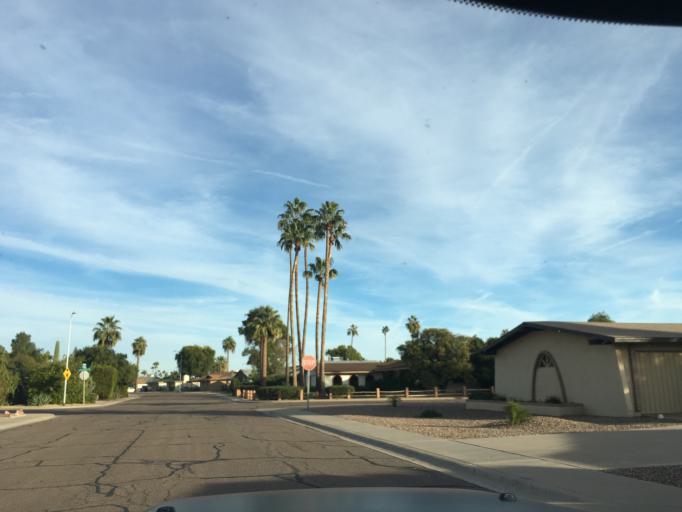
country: US
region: Arizona
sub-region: Maricopa County
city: Tempe
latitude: 33.3682
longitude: -111.9081
